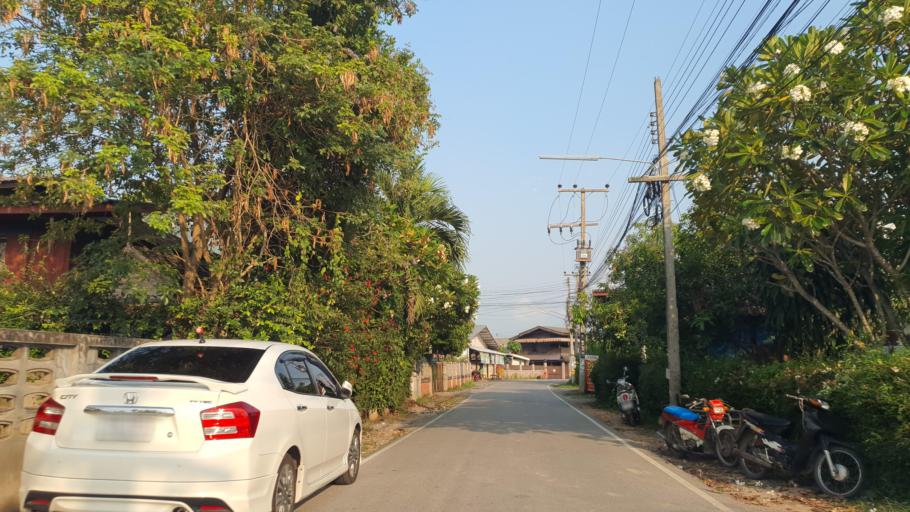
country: TH
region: Chiang Mai
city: San Pa Tong
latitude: 18.6376
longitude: 98.8616
